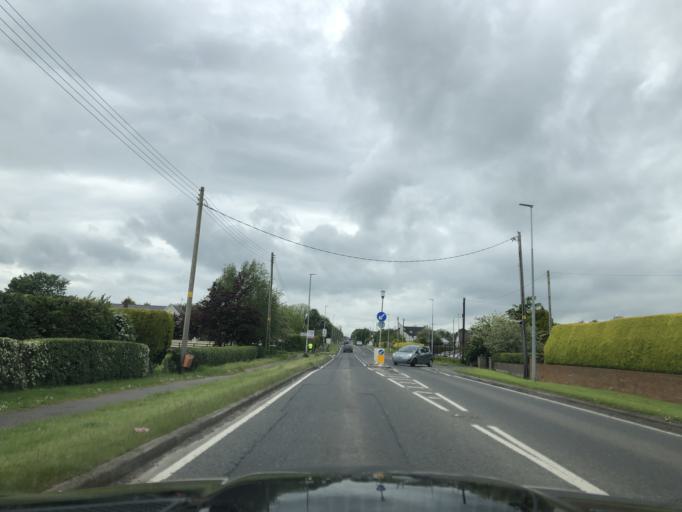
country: GB
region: Northern Ireland
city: Crossgar
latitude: 54.3652
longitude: -5.7779
